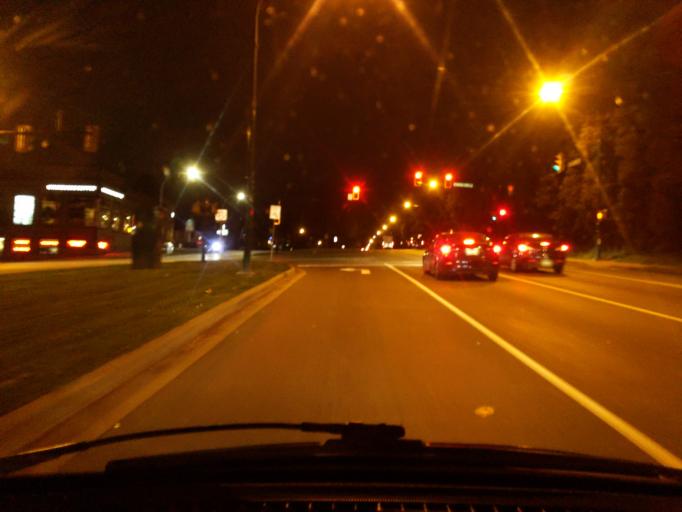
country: CA
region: British Columbia
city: Burnaby
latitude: 49.2551
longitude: -123.0237
